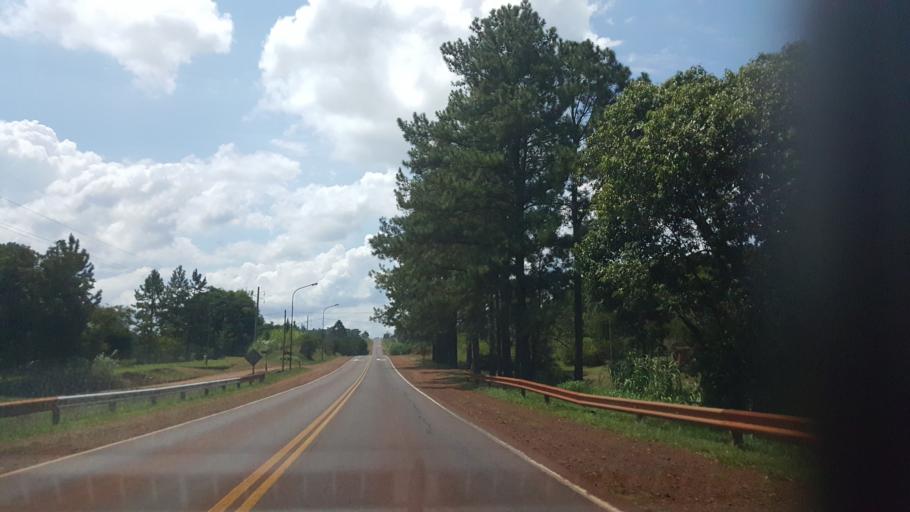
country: AR
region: Misiones
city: Puerto Rico
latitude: -26.8328
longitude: -55.0356
